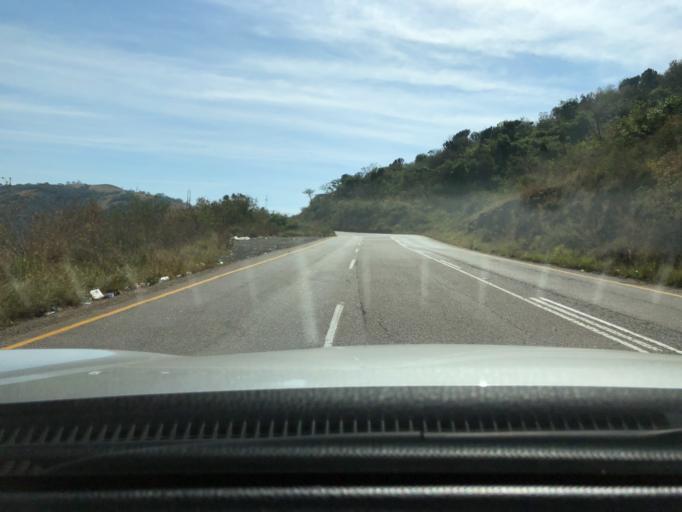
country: ZA
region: KwaZulu-Natal
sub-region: uMgungundlovu District Municipality
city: Richmond
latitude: -29.9973
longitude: 30.2460
